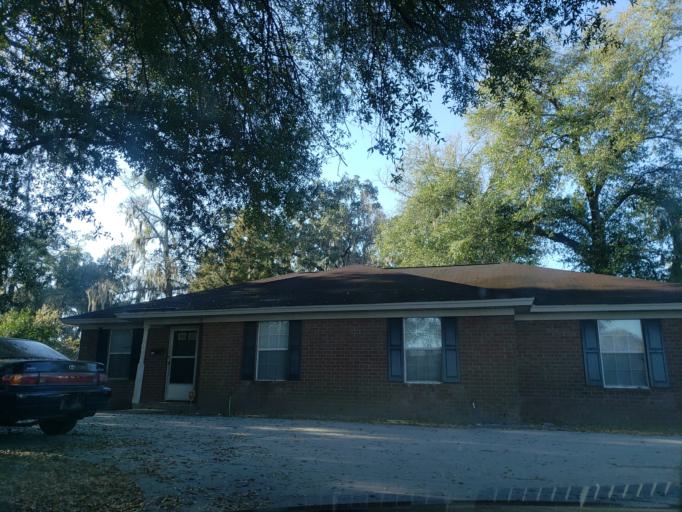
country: US
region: Georgia
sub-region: Chatham County
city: Thunderbolt
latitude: 32.0266
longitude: -81.0881
